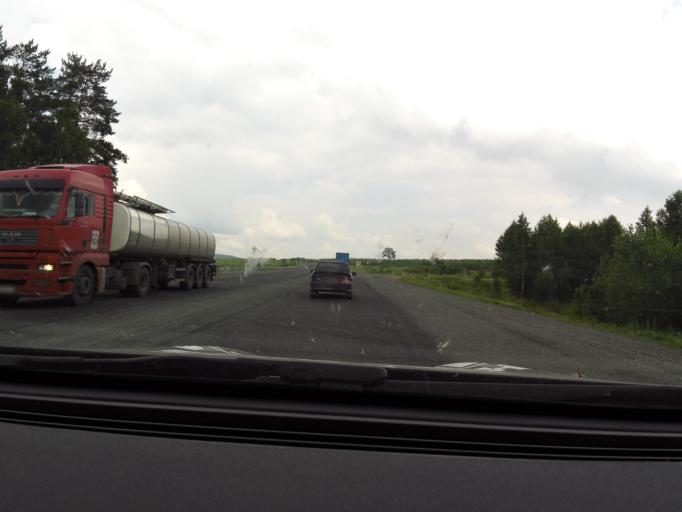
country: RU
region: Sverdlovsk
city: Ufimskiy
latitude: 56.7676
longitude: 58.1893
